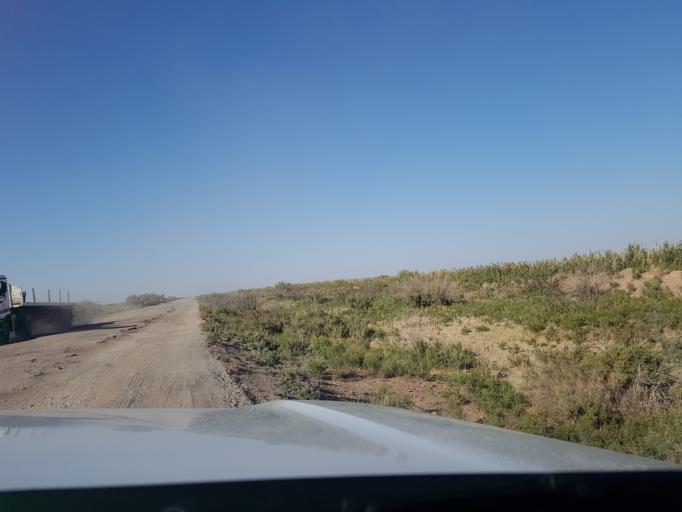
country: IR
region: Razavi Khorasan
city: Sarakhs
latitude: 36.9549
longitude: 61.3809
